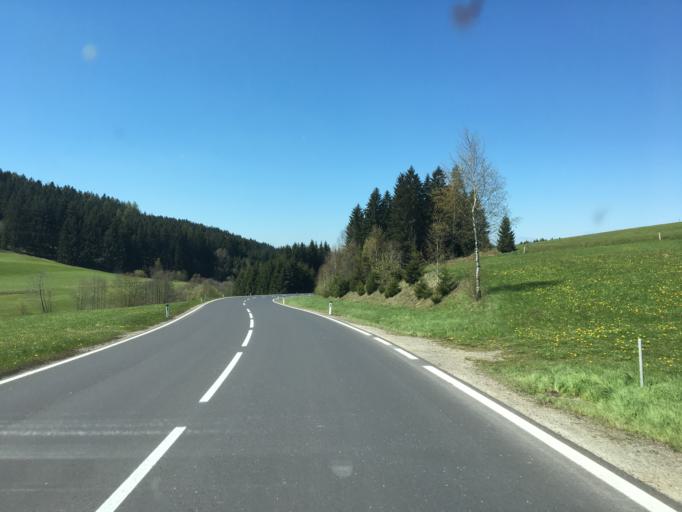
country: AT
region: Upper Austria
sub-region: Politischer Bezirk Urfahr-Umgebung
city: Hellmonsodt
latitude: 48.4381
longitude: 14.2929
